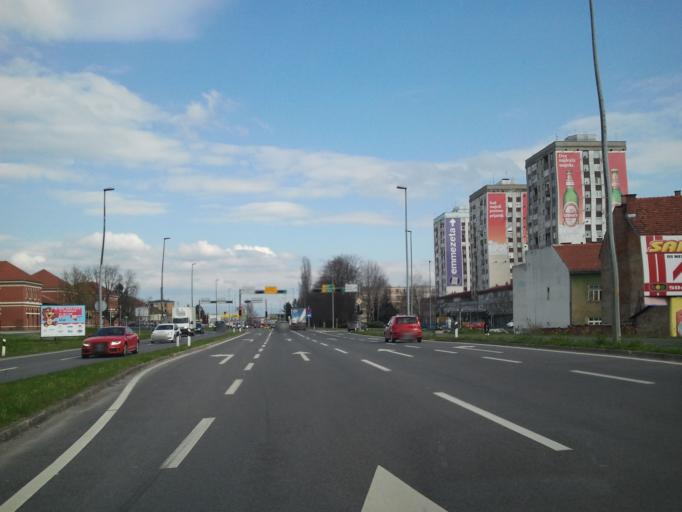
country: HR
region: Karlovacka
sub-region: Grad Karlovac
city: Karlovac
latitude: 45.4984
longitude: 15.5464
